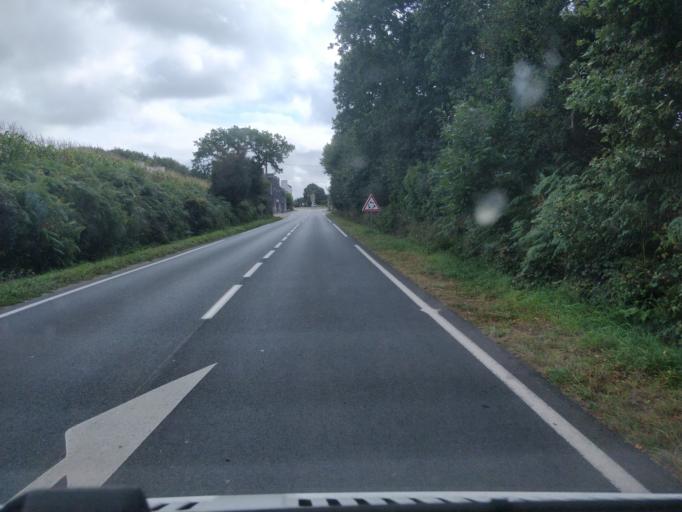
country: FR
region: Brittany
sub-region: Departement du Finistere
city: Plogastel-Saint-Germain
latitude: 47.9999
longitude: -4.2736
